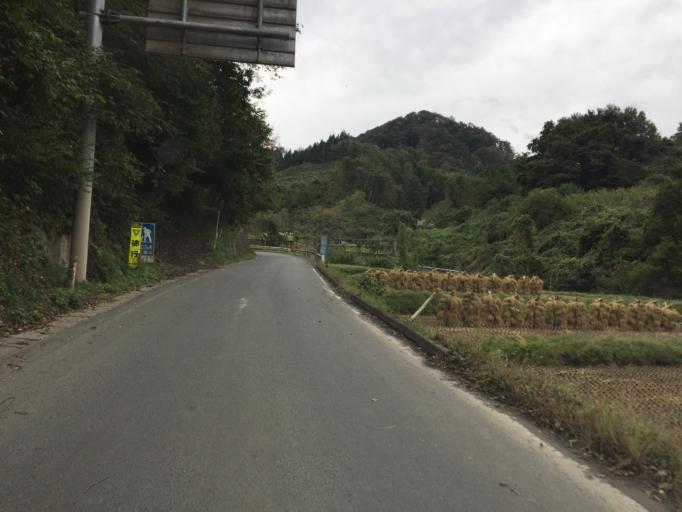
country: JP
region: Fukushima
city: Yanagawamachi-saiwaicho
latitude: 37.8806
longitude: 140.6829
